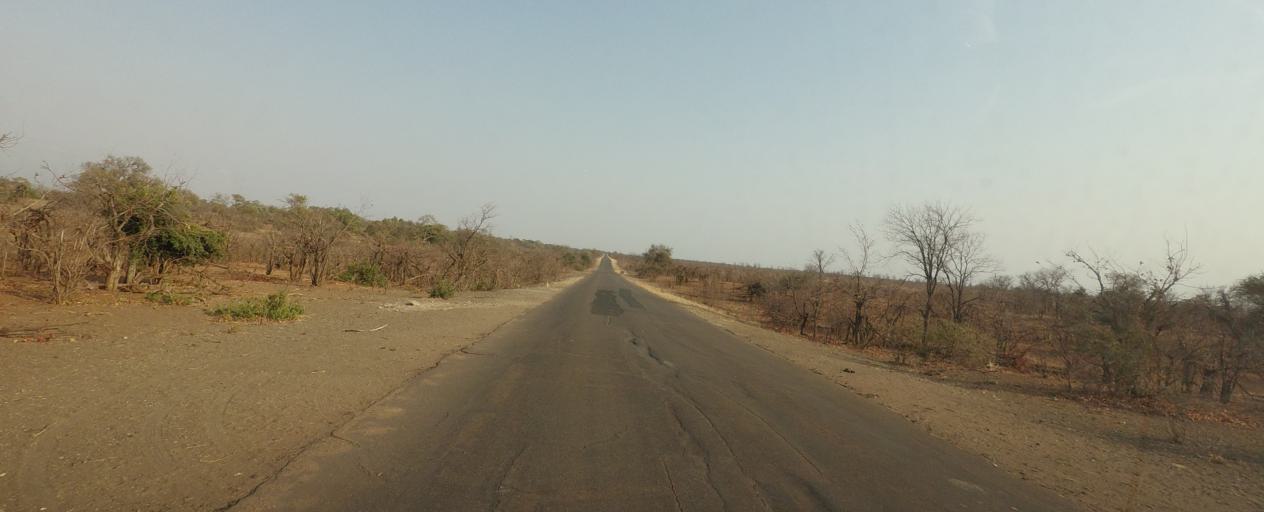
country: ZA
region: Limpopo
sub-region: Mopani District Municipality
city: Giyani
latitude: -23.0720
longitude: 31.4071
